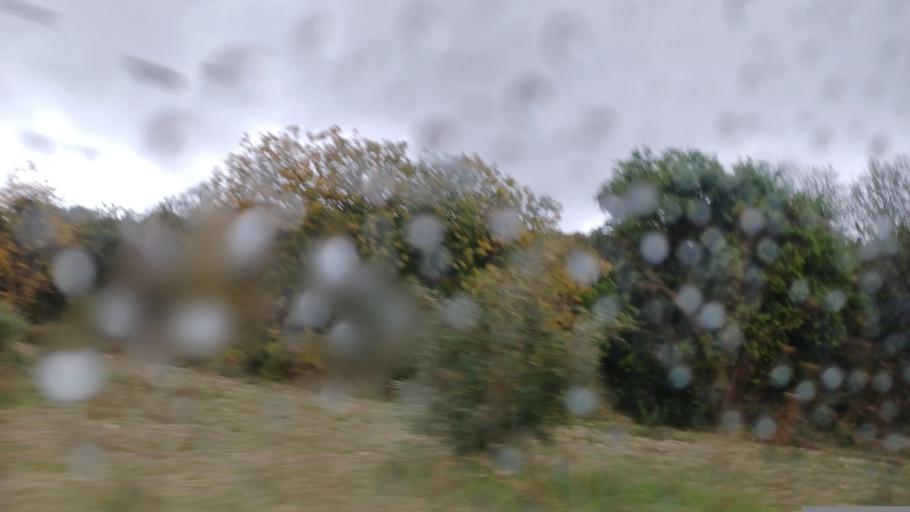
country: CY
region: Pafos
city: Mesogi
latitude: 34.8701
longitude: 32.5423
